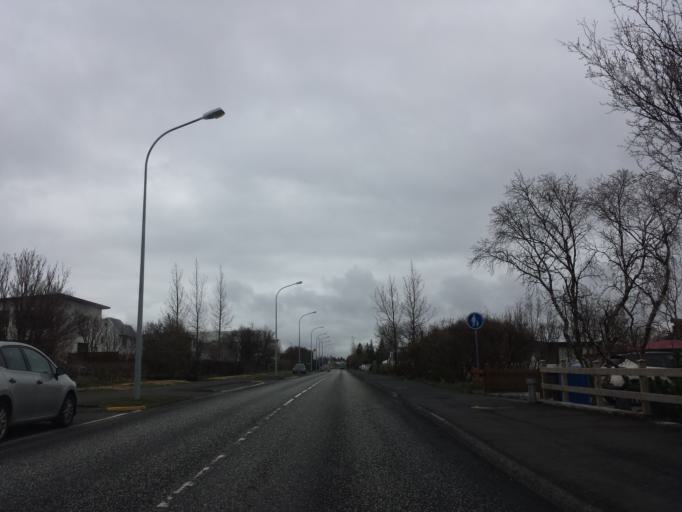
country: IS
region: Capital Region
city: Kopavogur
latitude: 64.1091
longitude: -21.9270
